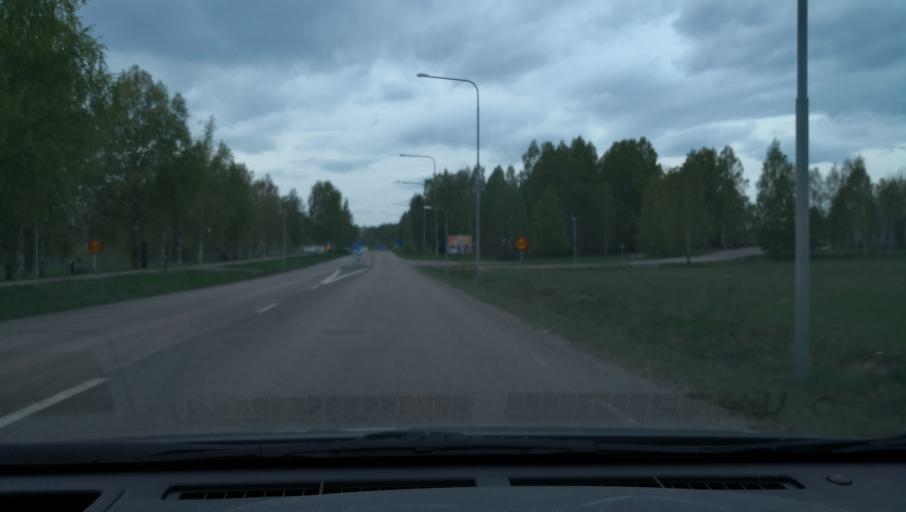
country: SE
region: Dalarna
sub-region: Avesta Kommun
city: Avesta
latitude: 60.1386
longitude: 16.2020
